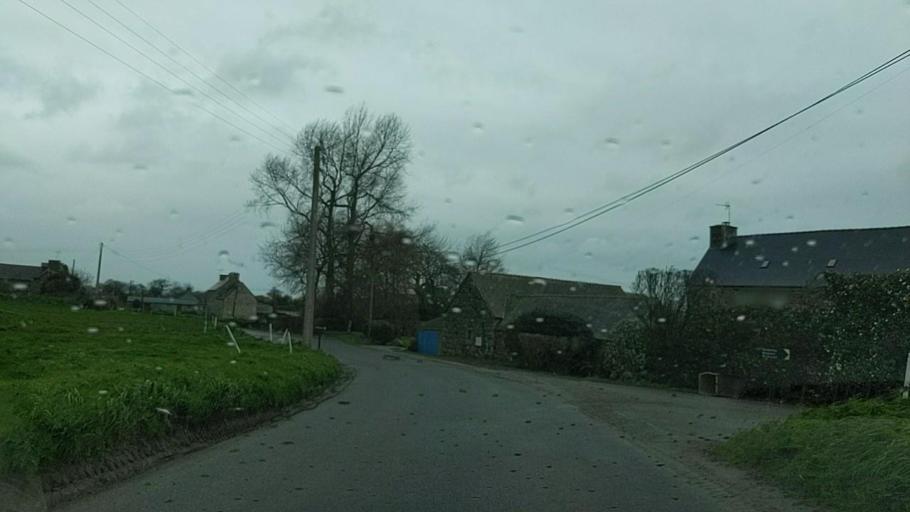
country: FR
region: Brittany
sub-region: Departement des Cotes-d'Armor
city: Pleumeur-Gautier
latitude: 48.8063
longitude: -3.1637
